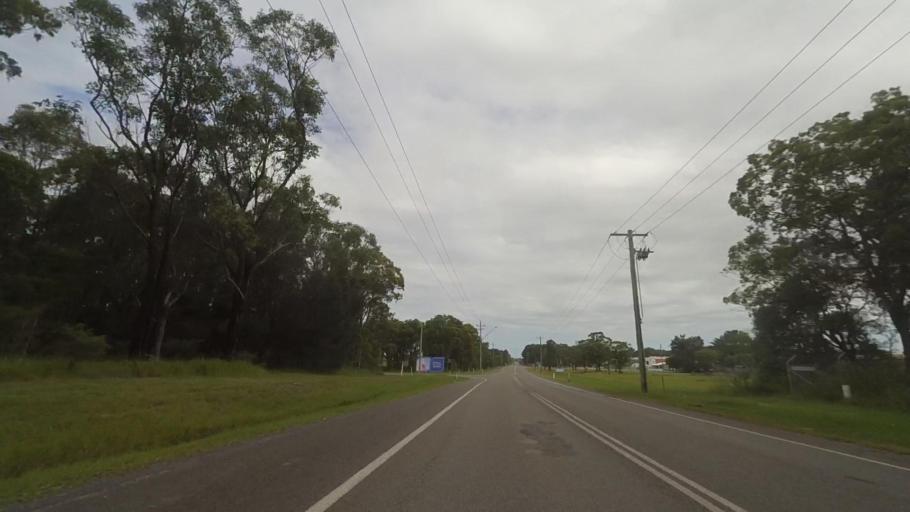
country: AU
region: New South Wales
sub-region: Great Lakes
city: Hawks Nest
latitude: -32.6430
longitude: 152.1459
